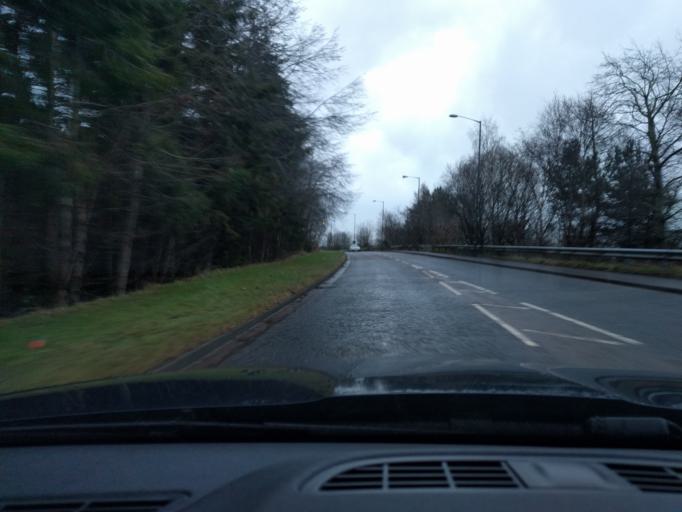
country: GB
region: Scotland
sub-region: Falkirk
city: Falkirk
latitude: 55.9894
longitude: -3.7539
